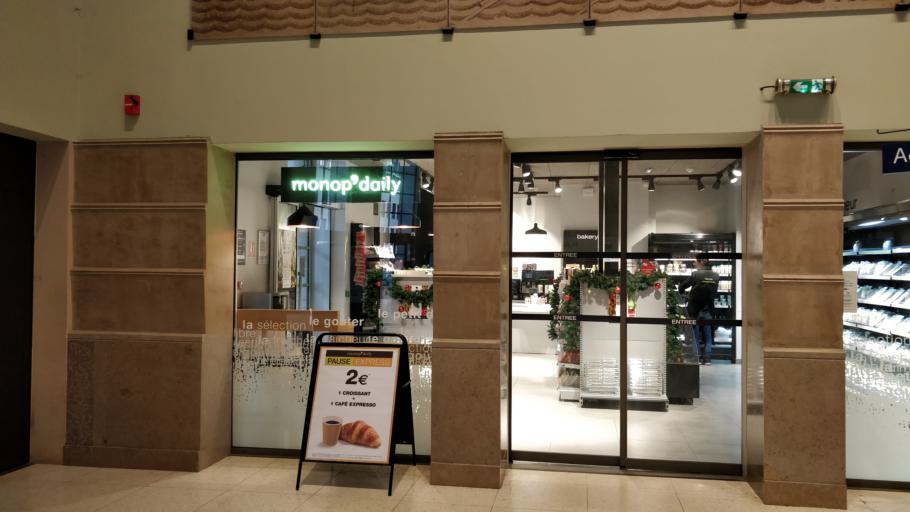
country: FR
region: Ile-de-France
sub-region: Departement des Yvelines
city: Versailles
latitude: 48.7958
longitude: 2.1359
